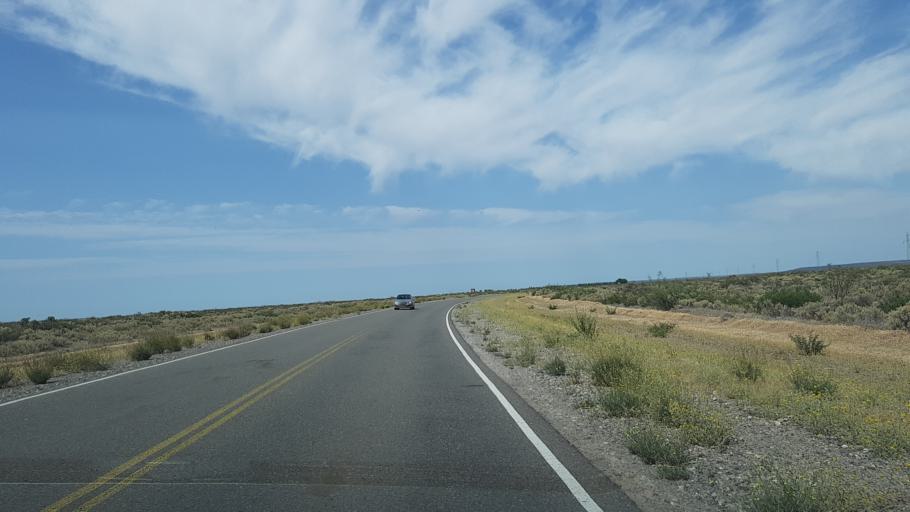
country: AR
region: Neuquen
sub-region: Departamento de Picun Leufu
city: Picun Leufu
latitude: -39.6263
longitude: -69.3600
